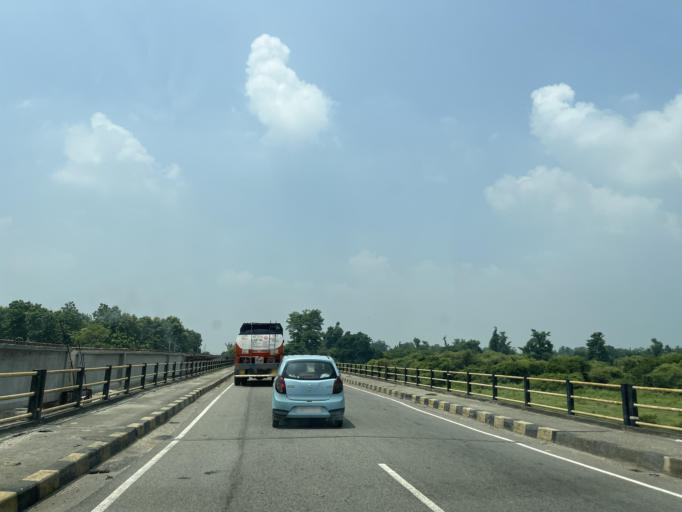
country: IN
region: Uttarakhand
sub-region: Haridwar
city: Haridwar
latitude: 29.8411
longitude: 78.1925
